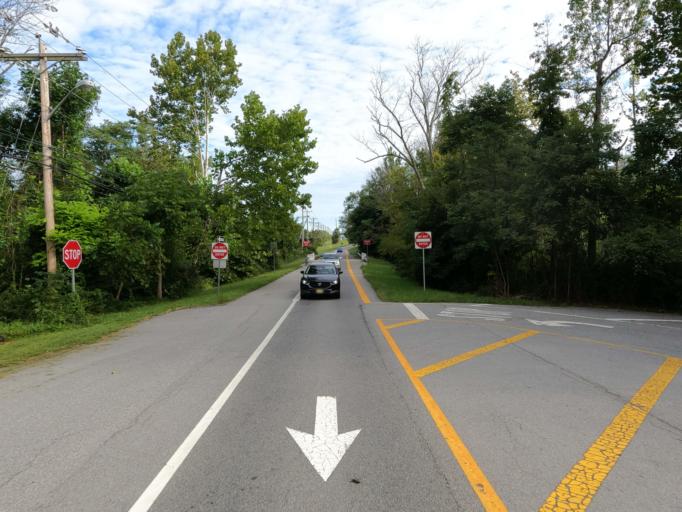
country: US
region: Delaware
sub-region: New Castle County
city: Glasgow
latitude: 39.6096
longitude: -75.7463
